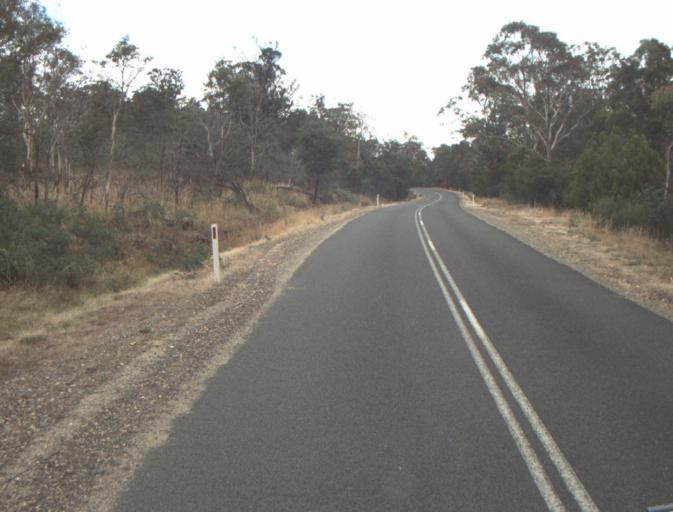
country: AU
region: Tasmania
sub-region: Northern Midlands
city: Evandale
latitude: -41.4956
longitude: 147.3875
